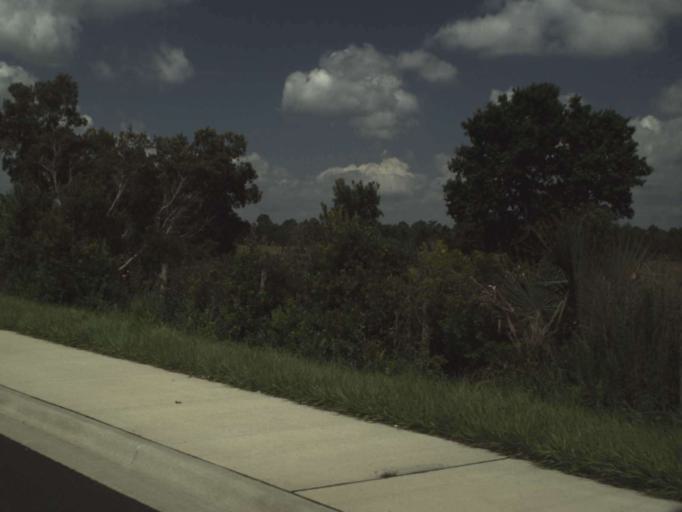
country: US
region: Florida
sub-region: Seminole County
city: Midway
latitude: 28.8275
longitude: -81.1791
